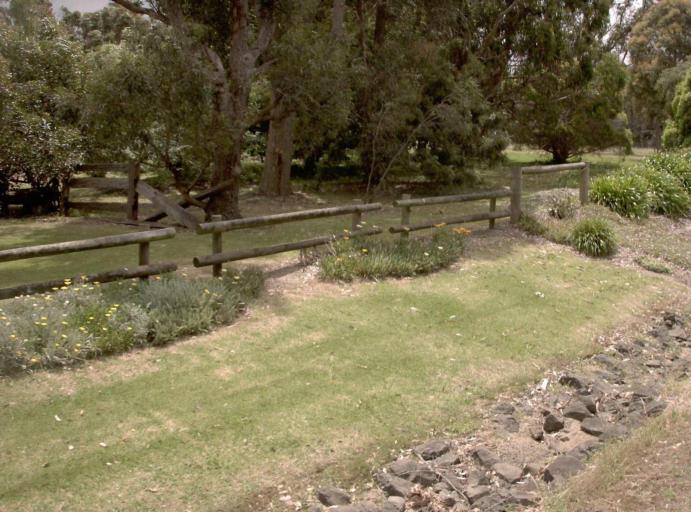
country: AU
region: Victoria
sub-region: Latrobe
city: Traralgon
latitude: -38.5428
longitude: 146.6562
